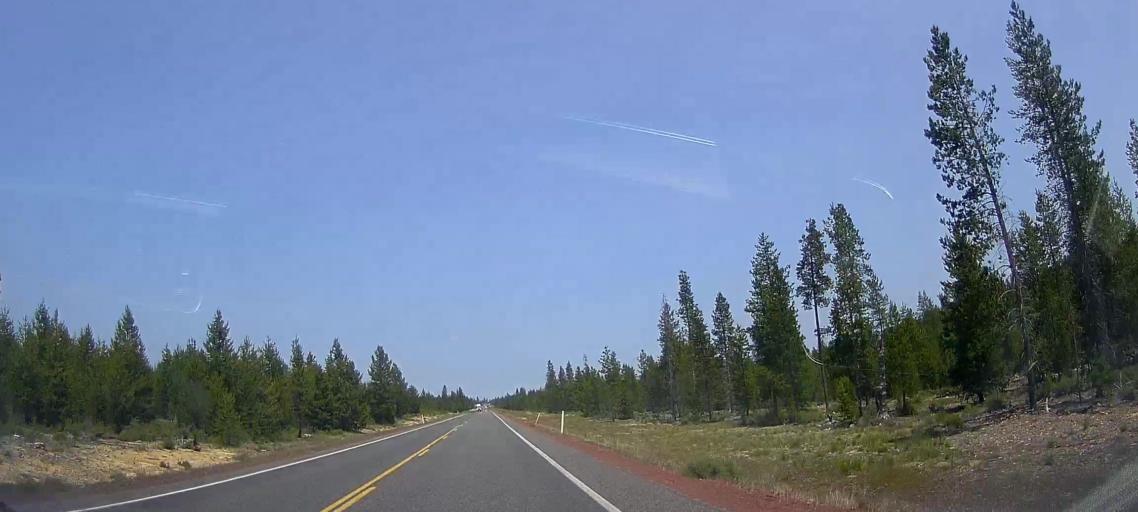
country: US
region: Oregon
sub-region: Deschutes County
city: La Pine
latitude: 43.3882
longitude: -121.7288
